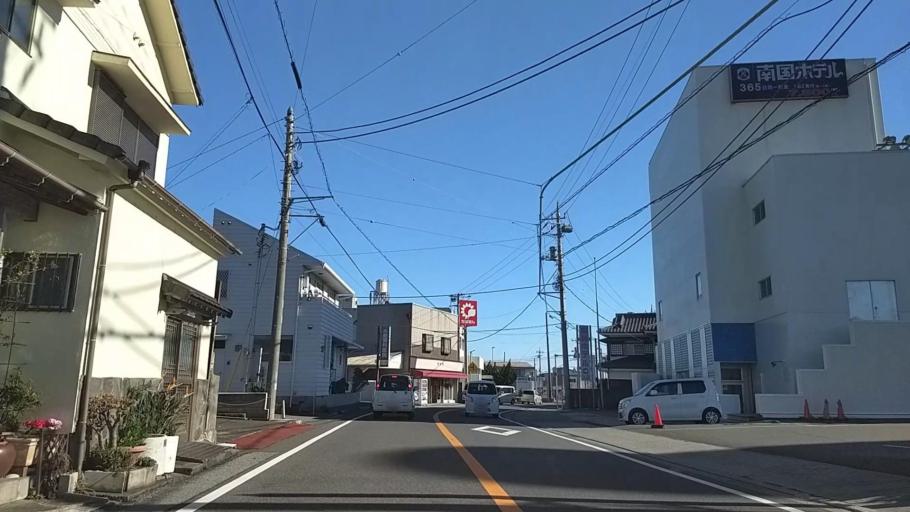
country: JP
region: Chiba
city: Tateyama
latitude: 34.9077
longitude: 139.8947
